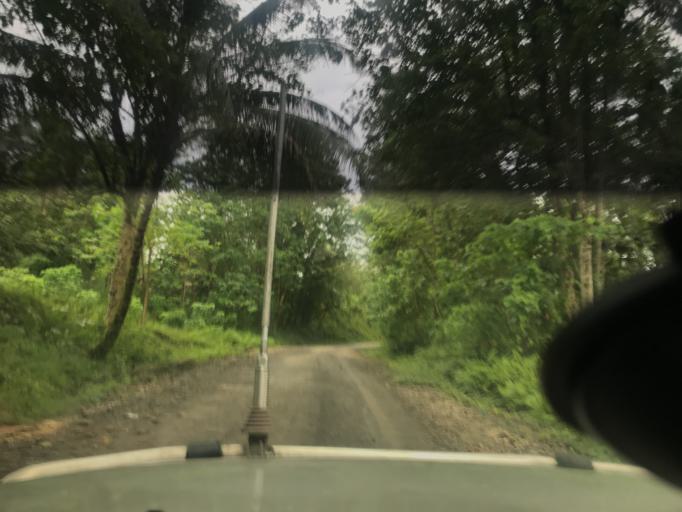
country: SB
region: Malaita
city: Auki
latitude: -8.9444
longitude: 160.7791
